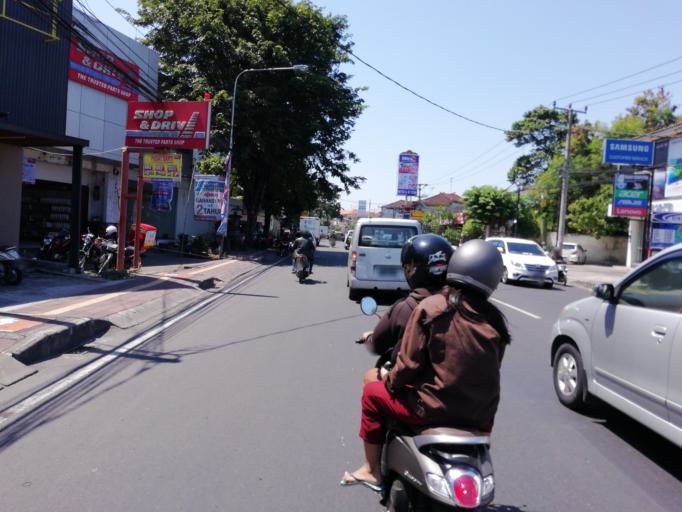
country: ID
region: Bali
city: Karyadharma
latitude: -8.6813
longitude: 115.1995
